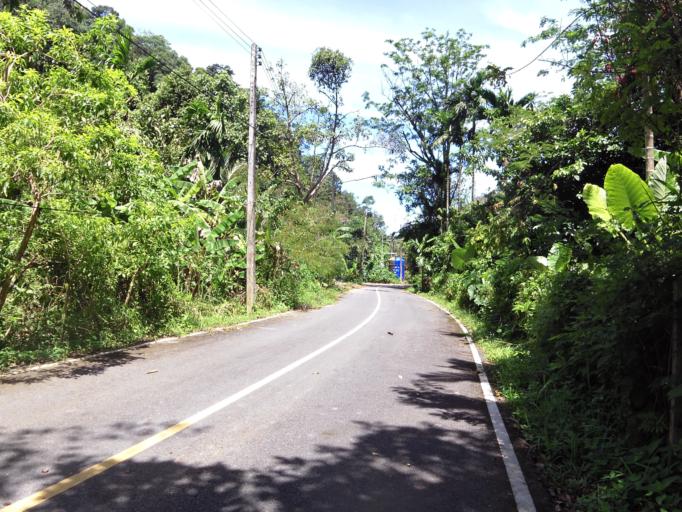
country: TH
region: Phuket
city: Ban Karon
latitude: 7.8452
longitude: 98.3099
